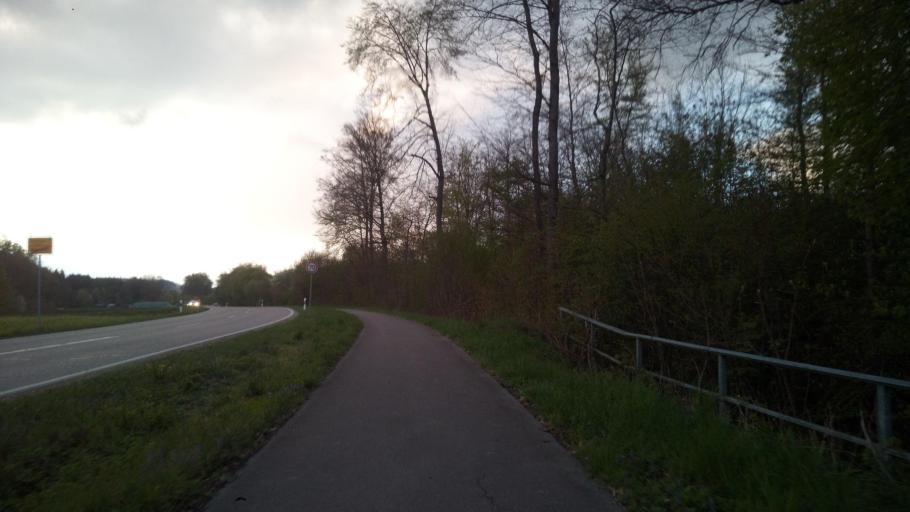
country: DE
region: Baden-Wuerttemberg
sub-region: Regierungsbezirk Stuttgart
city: Donzdorf
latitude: 48.7027
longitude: 9.8255
